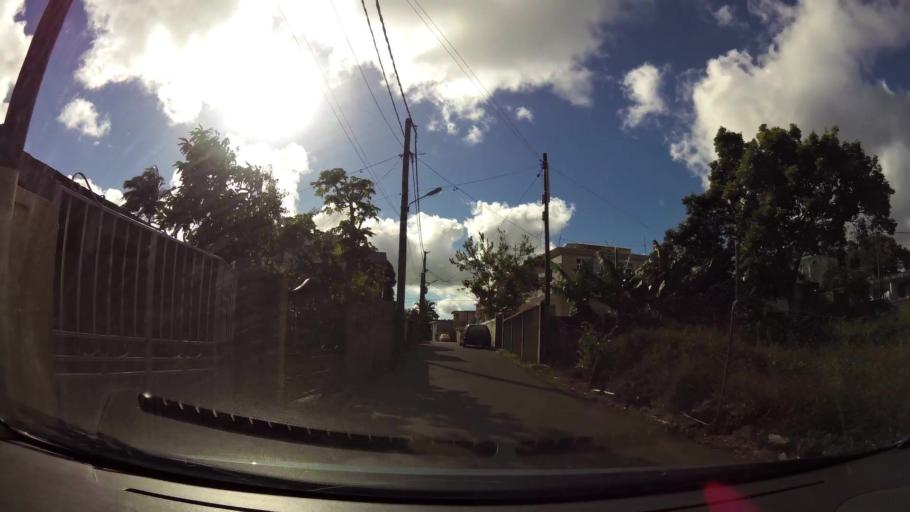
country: MU
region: Plaines Wilhems
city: Curepipe
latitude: -20.3027
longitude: 57.5178
